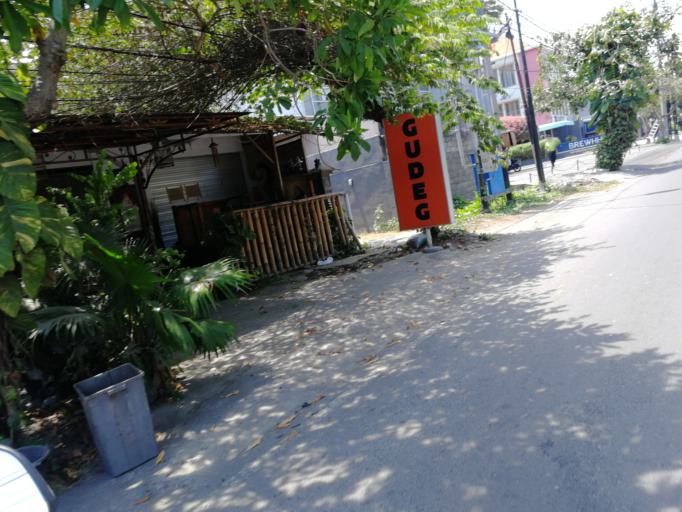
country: ID
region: Bali
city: Denpasar
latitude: -8.6640
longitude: 115.2304
